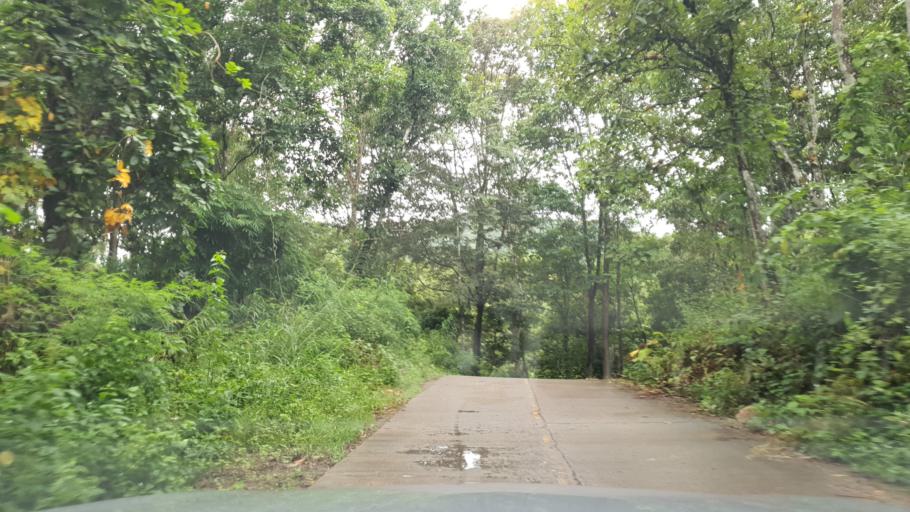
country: TH
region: Chiang Mai
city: Mae Taeng
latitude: 19.2154
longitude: 98.9266
